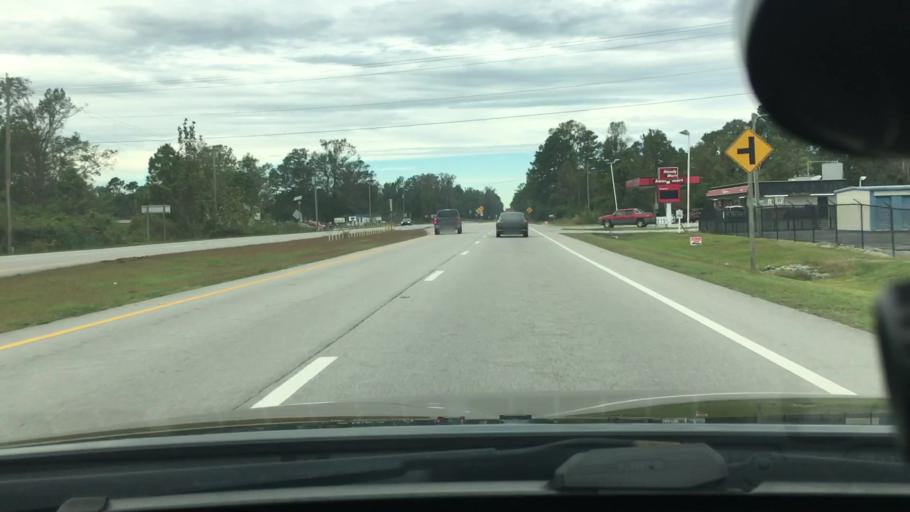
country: US
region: North Carolina
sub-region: Craven County
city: New Bern
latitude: 35.1544
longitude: -77.0355
